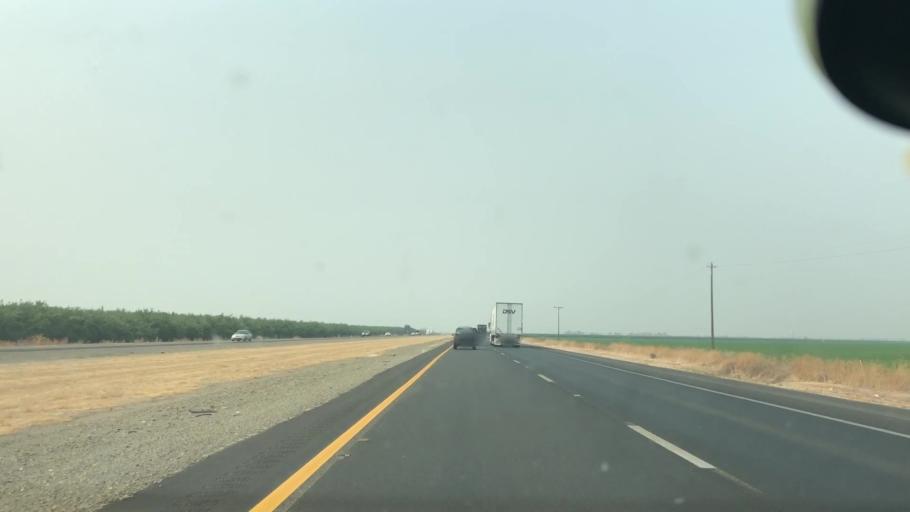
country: US
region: California
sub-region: San Joaquin County
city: Tracy
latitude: 37.7129
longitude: -121.3434
